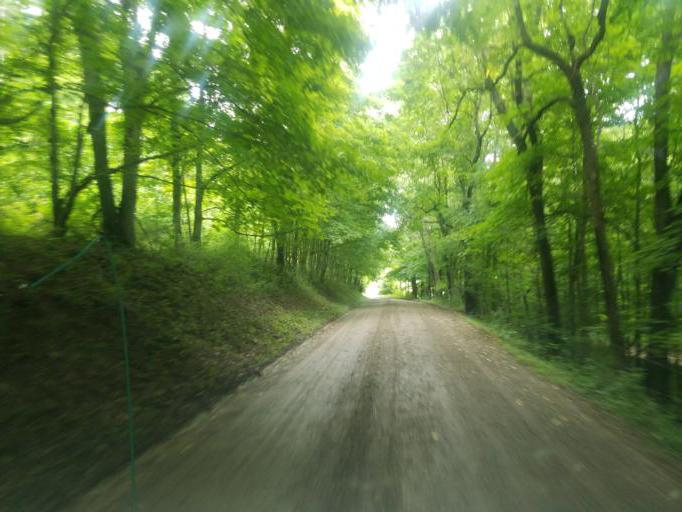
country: US
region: Ohio
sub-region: Knox County
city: Oak Hill
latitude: 40.3240
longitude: -82.1236
